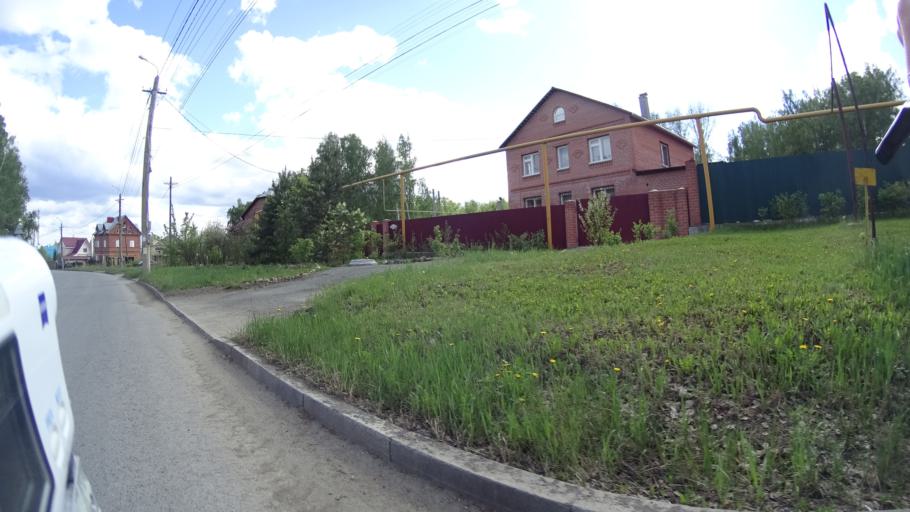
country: RU
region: Chelyabinsk
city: Sargazy
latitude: 55.1563
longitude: 61.2519
